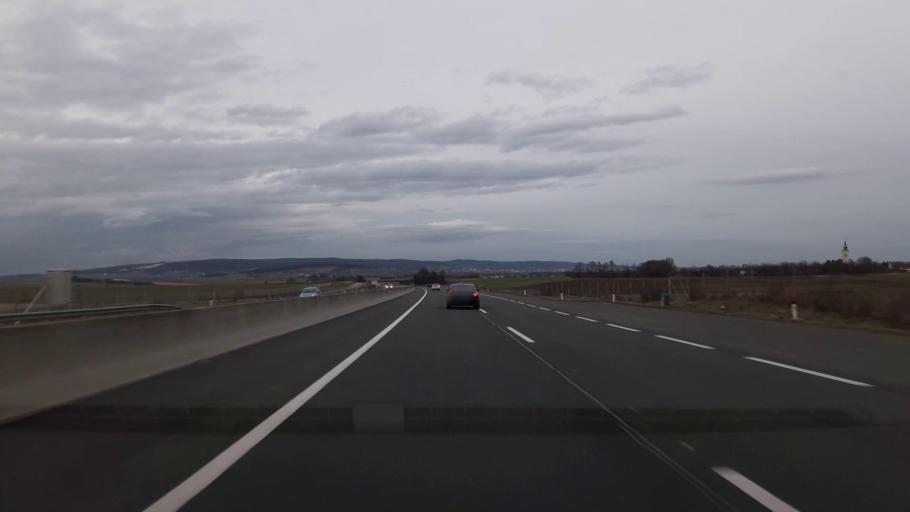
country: AT
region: Burgenland
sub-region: Politischer Bezirk Mattersburg
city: Pottelsdorf
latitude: 47.7694
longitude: 16.4272
